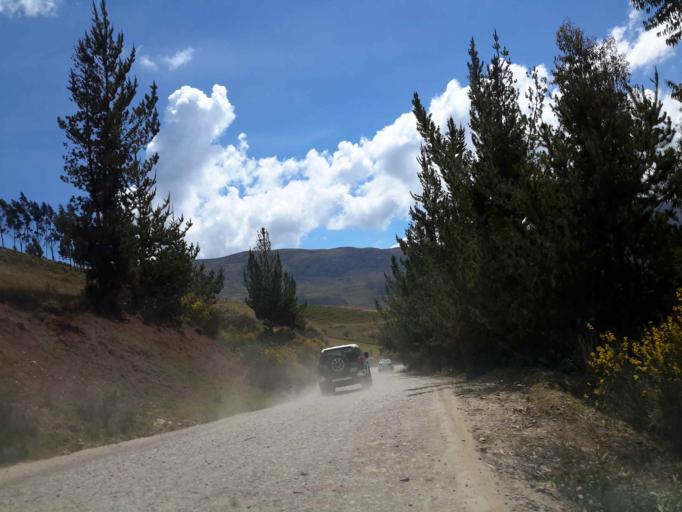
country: PE
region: Apurimac
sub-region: Provincia de Andahuaylas
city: Pacucha
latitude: -13.6250
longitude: -73.3381
